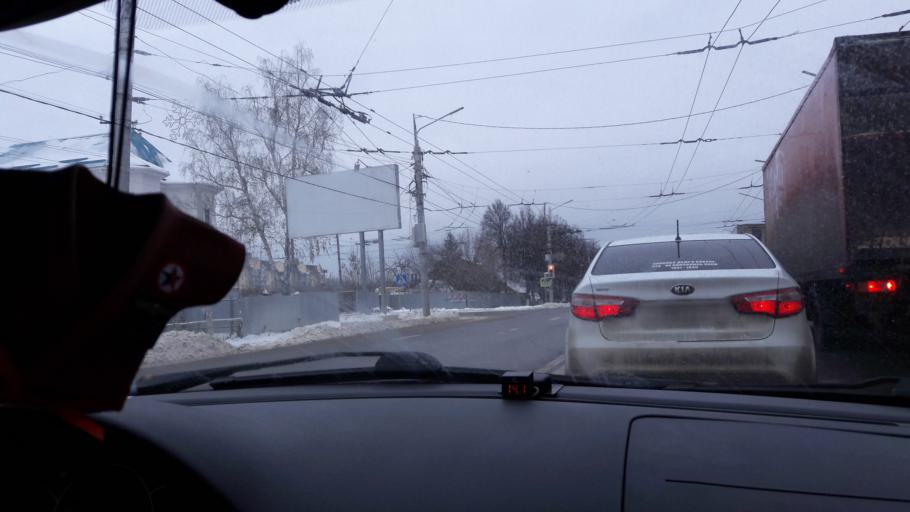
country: RU
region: Tula
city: Gorelki
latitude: 54.2345
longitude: 37.6235
